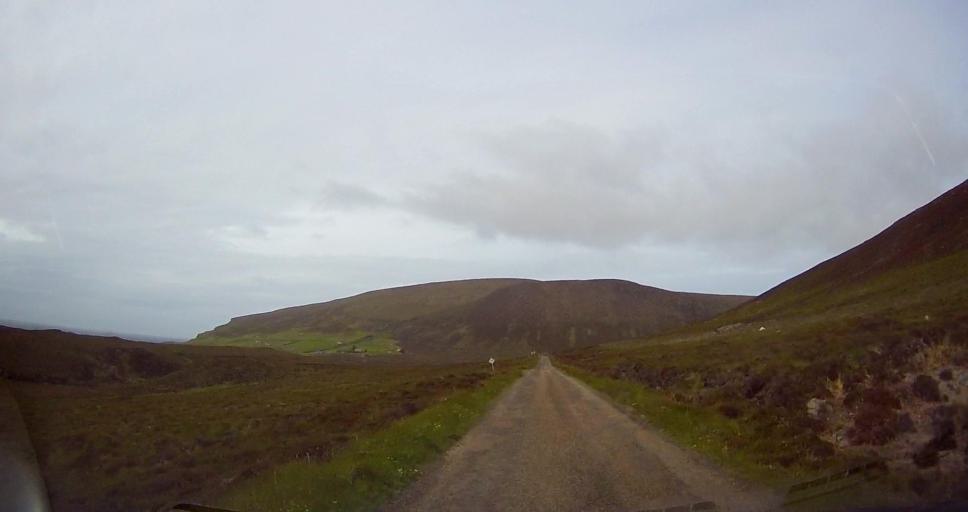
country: GB
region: Scotland
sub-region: Orkney Islands
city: Stromness
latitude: 58.8818
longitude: -3.3675
